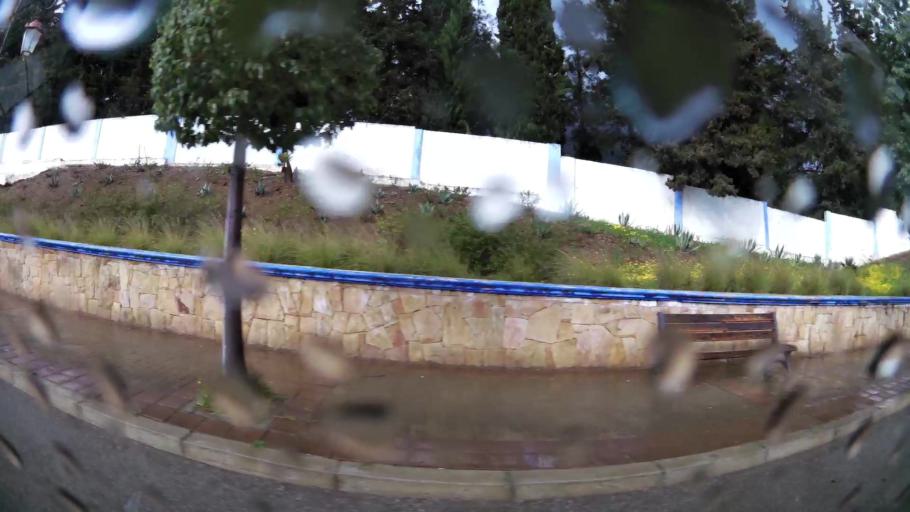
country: MA
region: Tanger-Tetouan
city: Chefchaouene
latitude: 35.1736
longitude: -5.2778
